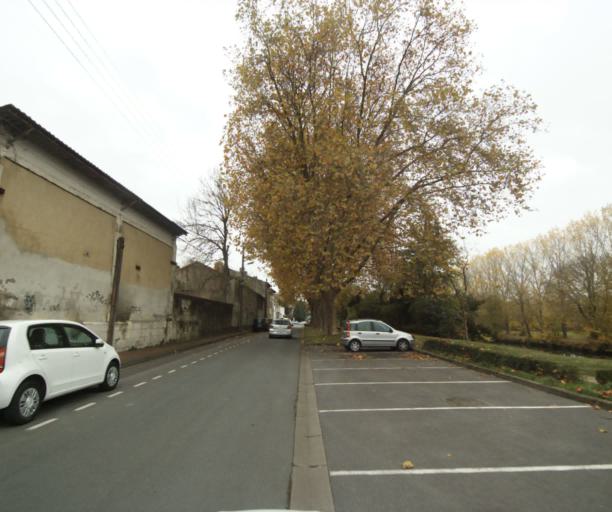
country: FR
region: Poitou-Charentes
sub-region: Departement de la Charente-Maritime
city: Saintes
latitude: 45.7399
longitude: -0.6378
